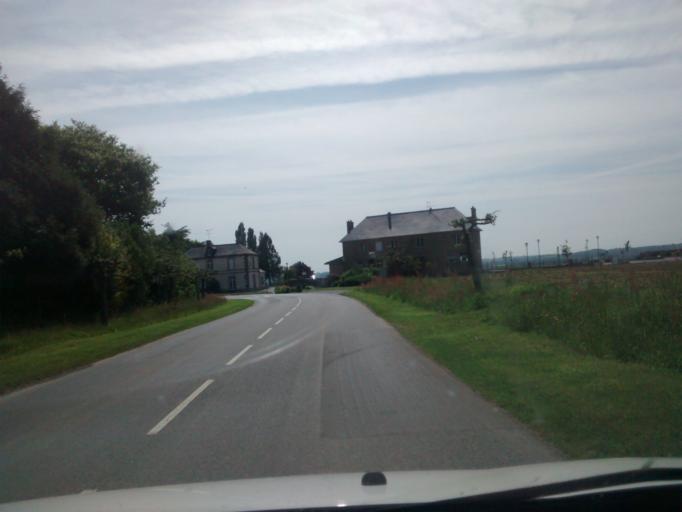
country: FR
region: Brittany
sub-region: Departement d'Ille-et-Vilaine
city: Antrain
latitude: 48.4665
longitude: -1.5059
